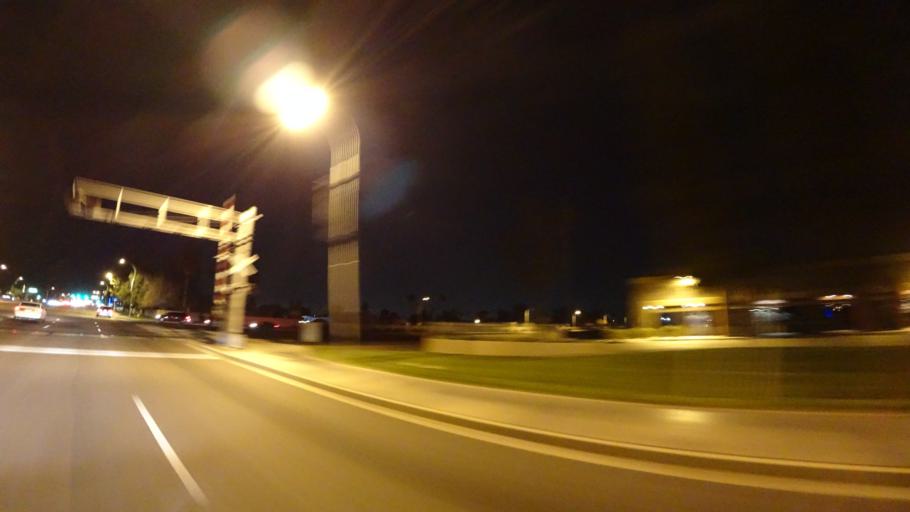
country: US
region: Arizona
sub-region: Maricopa County
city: Guadalupe
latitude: 33.3783
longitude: -111.9432
